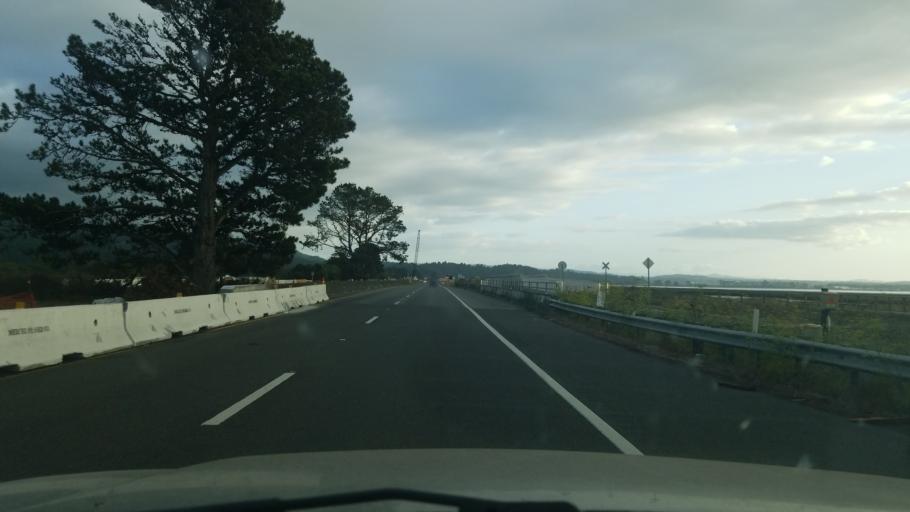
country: US
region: California
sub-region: Humboldt County
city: Arcata
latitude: 40.8477
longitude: -124.0821
